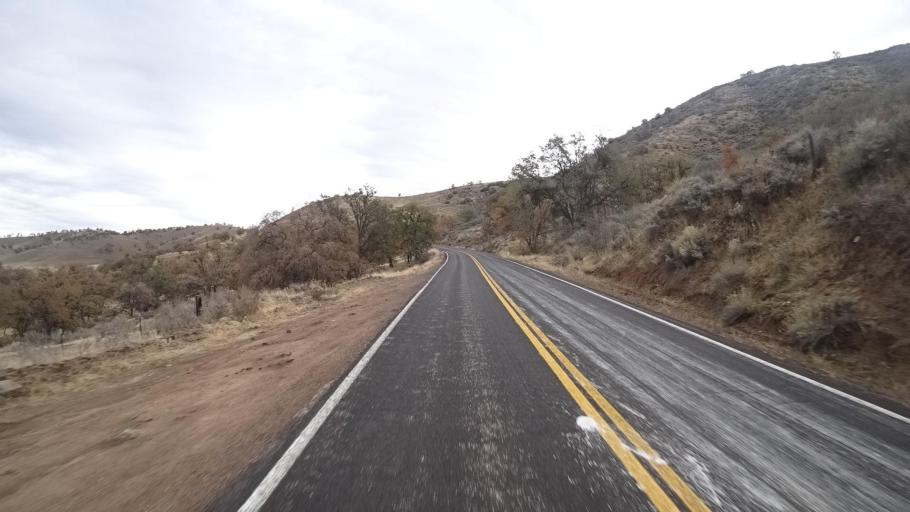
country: US
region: California
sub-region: Kern County
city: Stallion Springs
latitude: 35.0907
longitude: -118.5599
